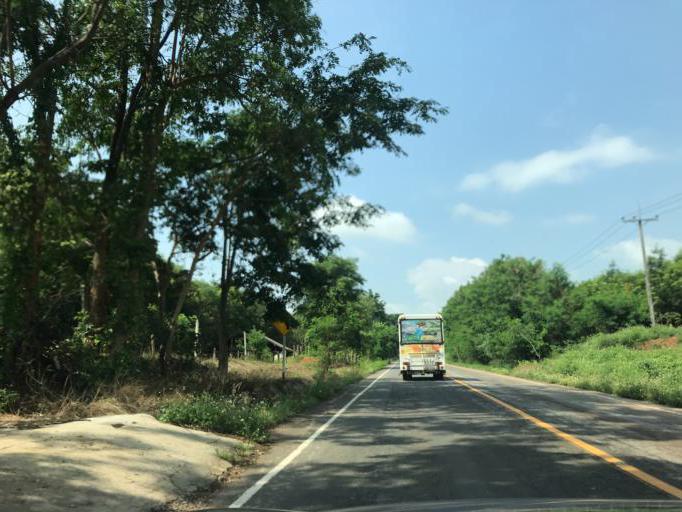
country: TH
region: Phayao
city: Chiang Kham
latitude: 19.4420
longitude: 100.3088
